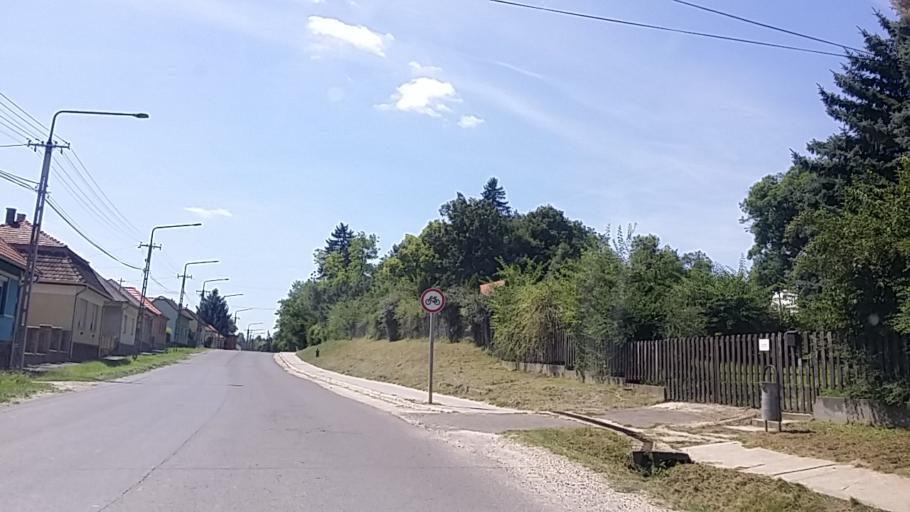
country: HU
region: Somogy
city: Tab
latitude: 46.7285
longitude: 18.0273
